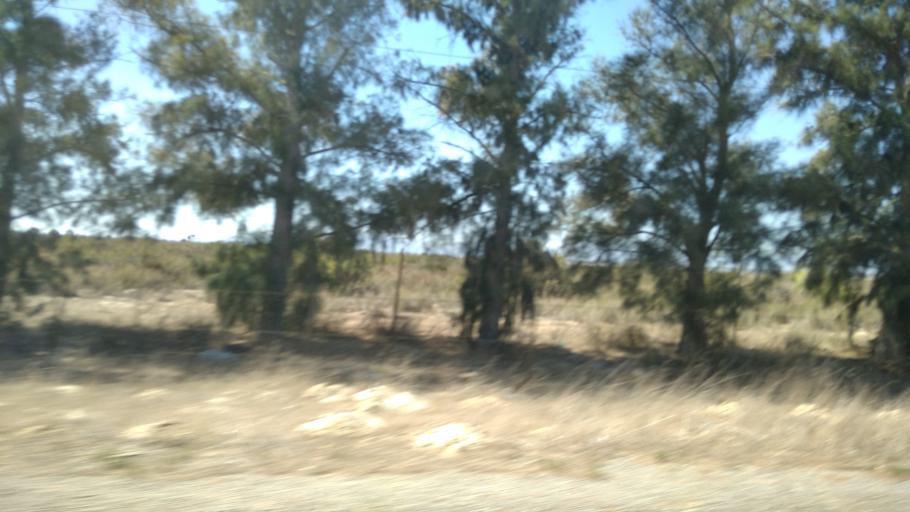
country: ZA
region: Western Cape
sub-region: West Coast District Municipality
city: Moorreesburg
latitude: -33.0462
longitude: 18.3222
